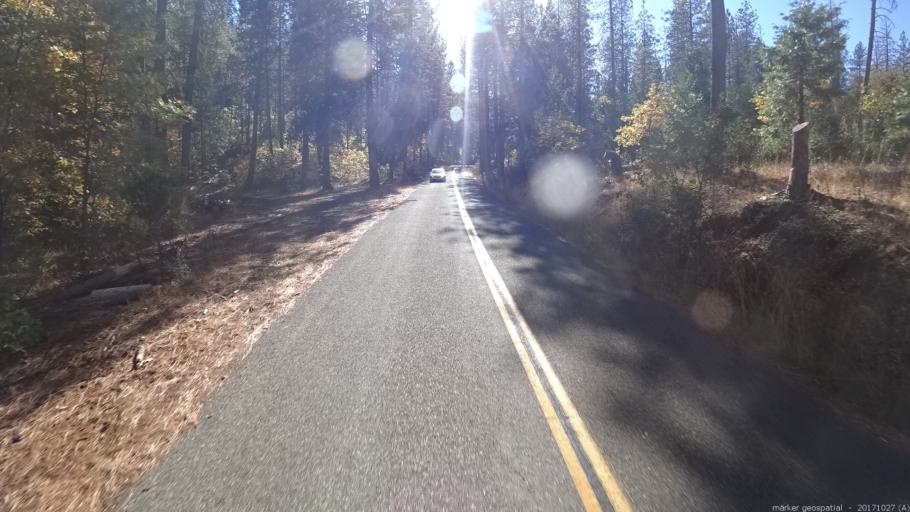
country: US
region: California
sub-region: Shasta County
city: Shingletown
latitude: 40.7187
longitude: -121.9856
